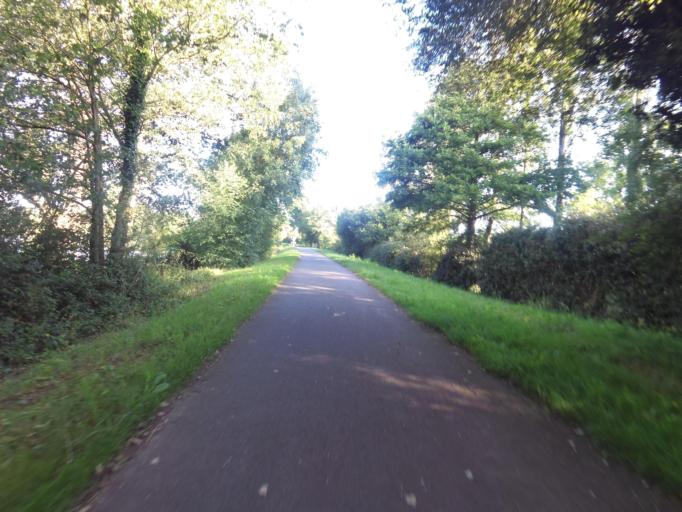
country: FR
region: Brittany
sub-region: Departement du Morbihan
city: Malestroit
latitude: 47.8347
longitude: -2.4229
